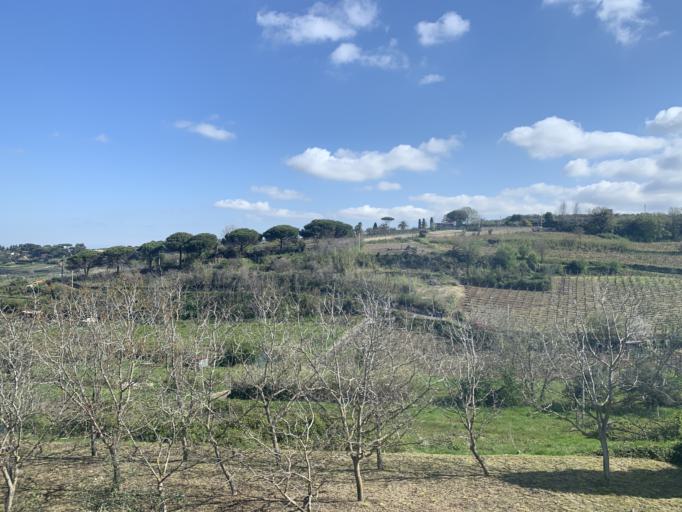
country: IT
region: Latium
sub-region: Citta metropolitana di Roma Capitale
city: Grottaferrata
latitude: 41.7839
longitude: 12.6506
